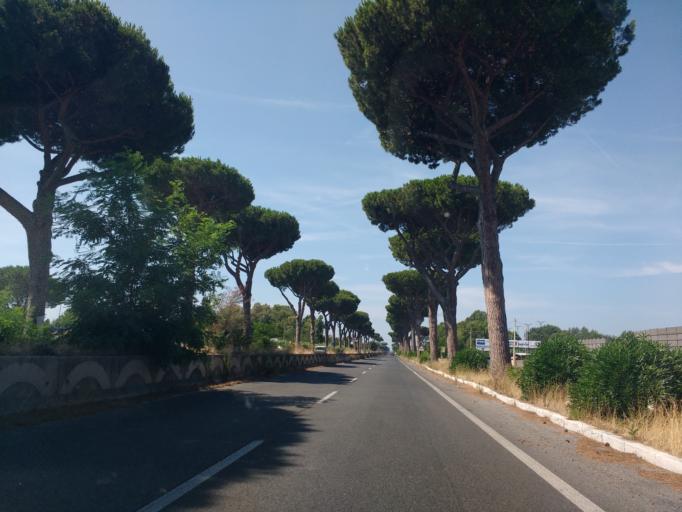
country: IT
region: Latium
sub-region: Citta metropolitana di Roma Capitale
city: Acilia-Castel Fusano-Ostia Antica
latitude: 41.7329
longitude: 12.3410
